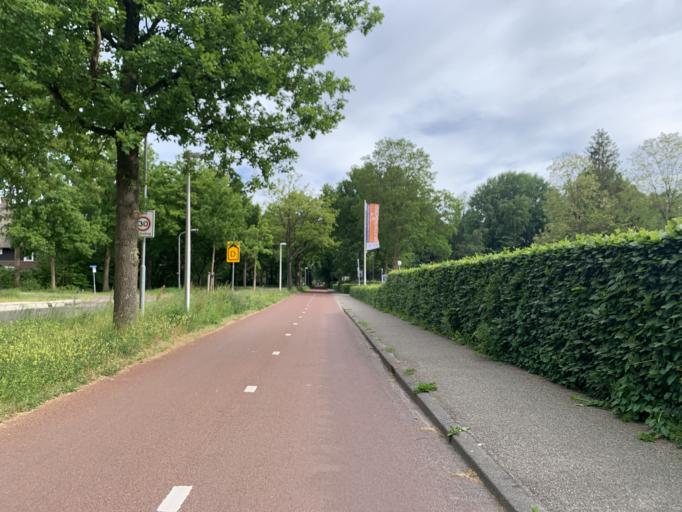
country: NL
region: Groningen
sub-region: Gemeente Haren
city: Haren
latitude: 53.1835
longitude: 6.6020
